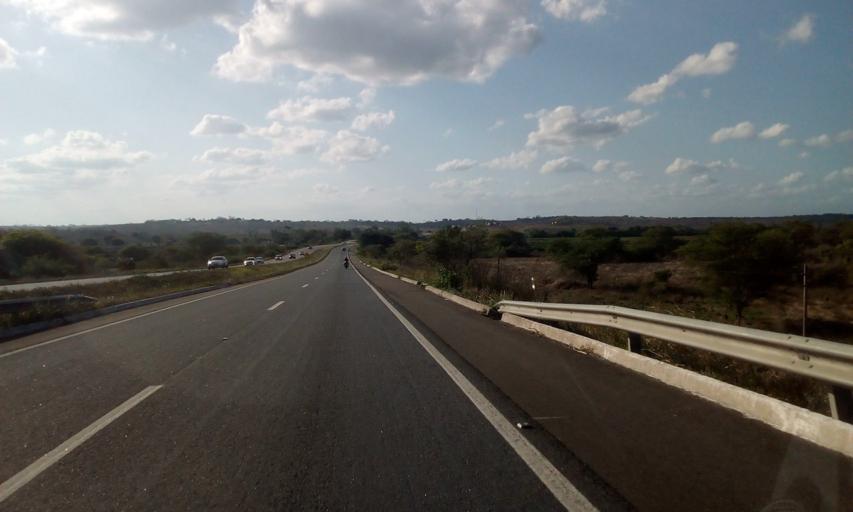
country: BR
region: Paraiba
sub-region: Cruz Do Espirito Santo
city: Cruz do Espirito Santo
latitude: -7.1920
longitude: -35.1811
